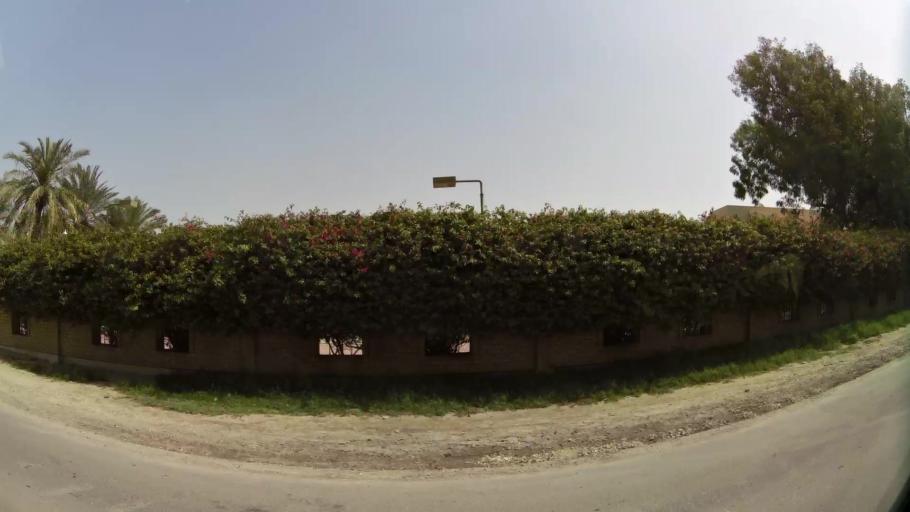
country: BH
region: Manama
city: Jidd Hafs
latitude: 26.2226
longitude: 50.4838
